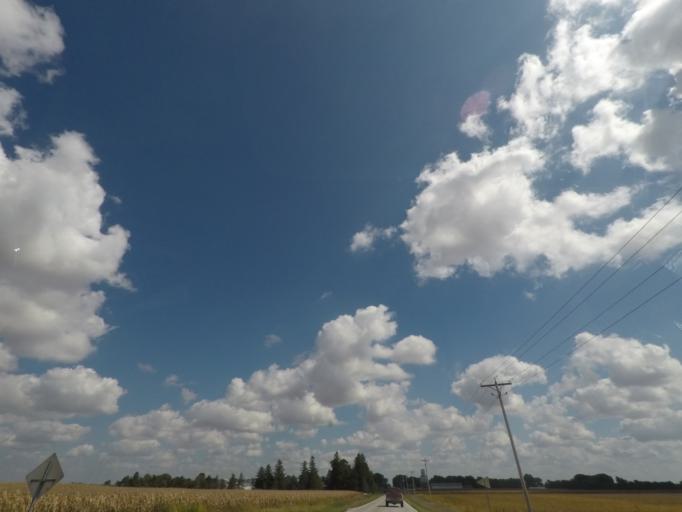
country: US
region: Iowa
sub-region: Story County
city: Nevada
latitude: 42.0706
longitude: -93.4037
